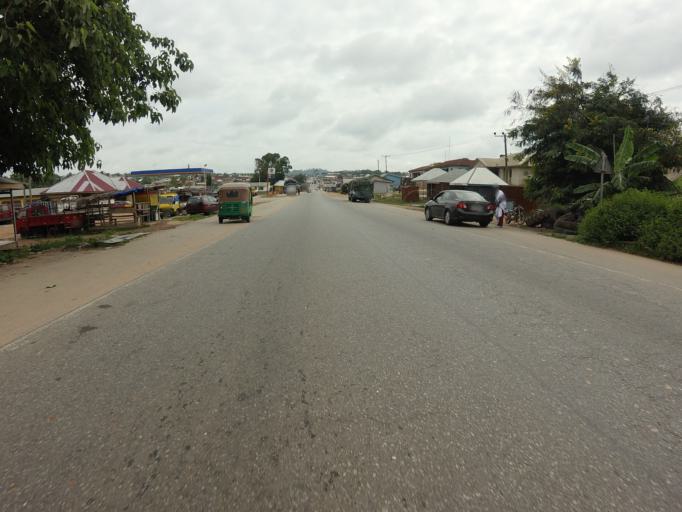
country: GH
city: Bechem
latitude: 7.1279
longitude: -1.7343
